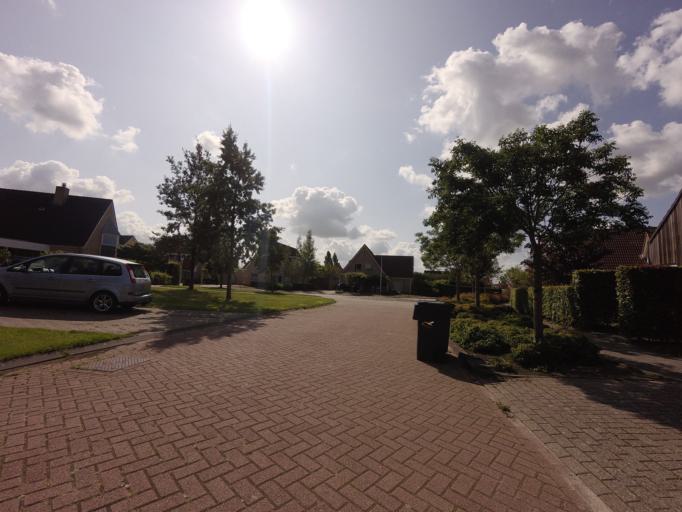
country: NL
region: Friesland
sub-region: Gemeente Het Bildt
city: Sint Annaparochie
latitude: 53.2808
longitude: 5.6610
